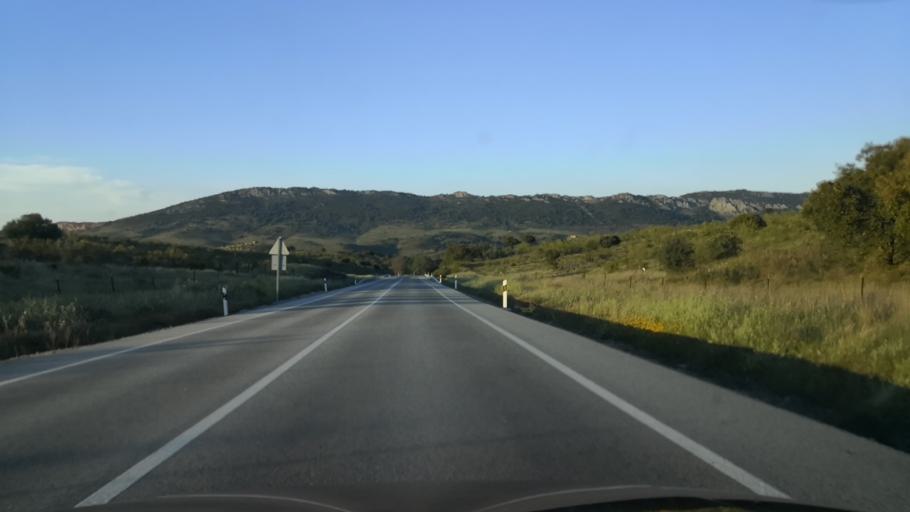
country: ES
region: Extremadura
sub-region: Provincia de Caceres
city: Valencia de Alcantara
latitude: 39.4534
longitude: -7.2094
